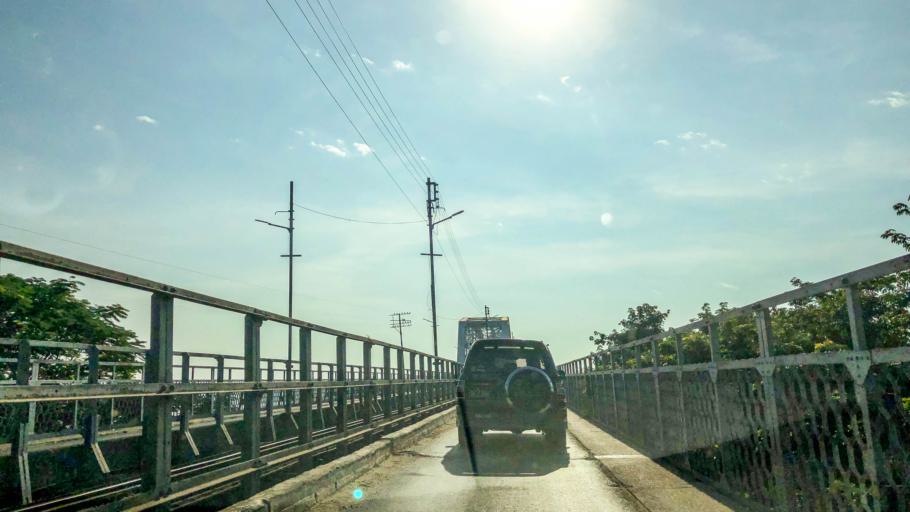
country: MM
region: Sagain
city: Sagaing
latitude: 21.8752
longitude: 95.9875
